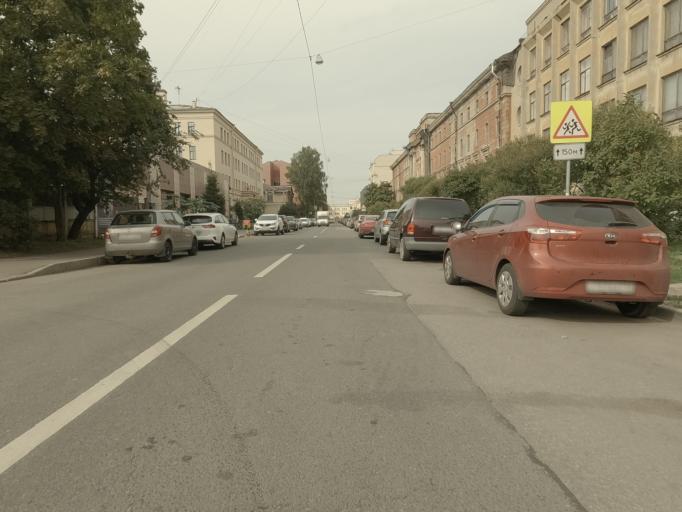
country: RU
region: St.-Petersburg
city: Admiralteisky
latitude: 59.9100
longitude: 30.2926
